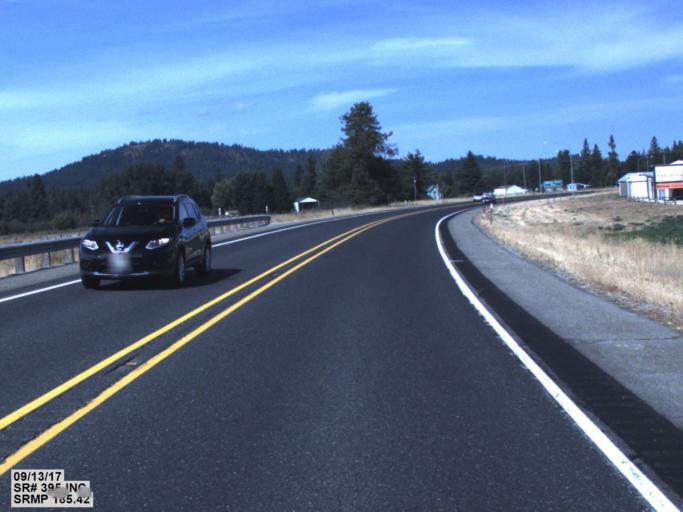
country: US
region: Washington
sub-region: Spokane County
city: Deer Park
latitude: 47.9950
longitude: -117.5700
